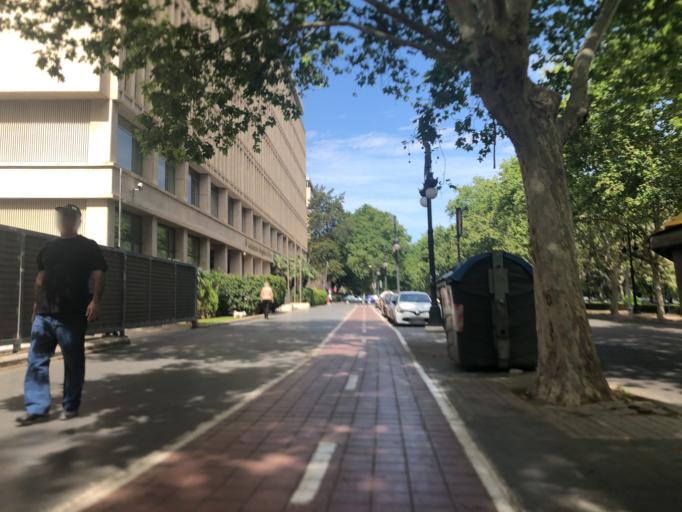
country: ES
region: Valencia
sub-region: Provincia de Valencia
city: Valencia
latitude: 39.4764
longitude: -0.3572
